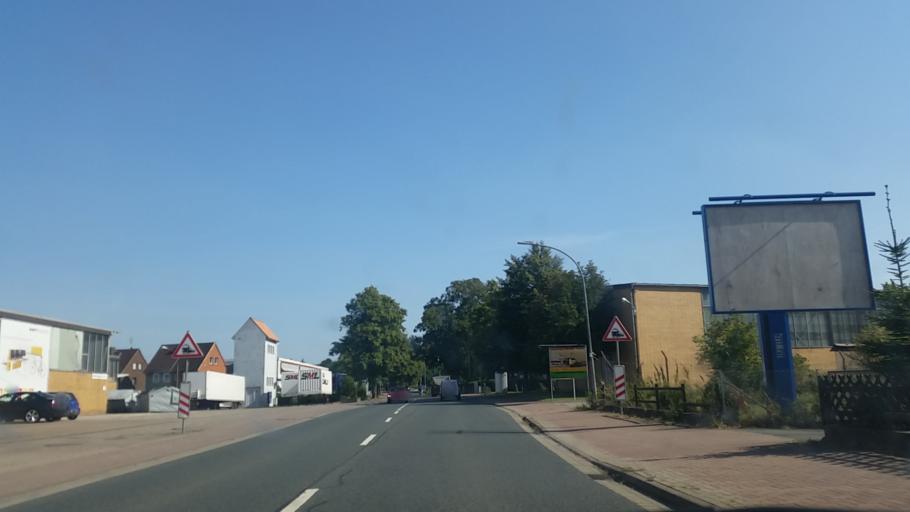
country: DE
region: Lower Saxony
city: Coppenbrugge
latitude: 52.1066
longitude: 9.5720
